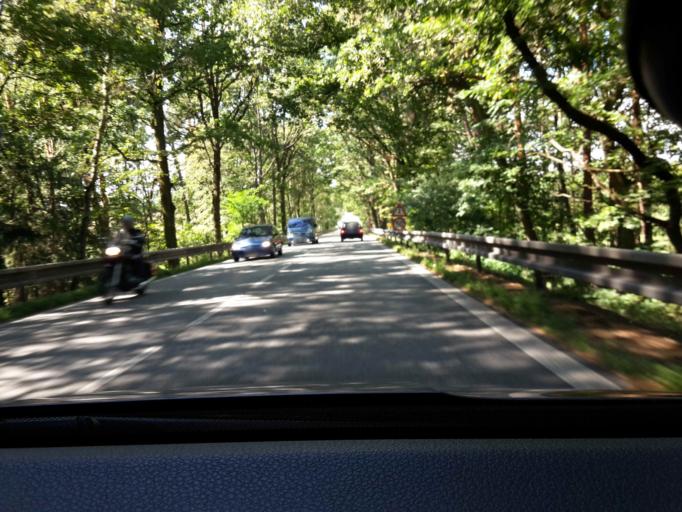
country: CZ
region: Jihocesky
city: Kardasova Recice
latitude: 49.1750
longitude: 14.8833
